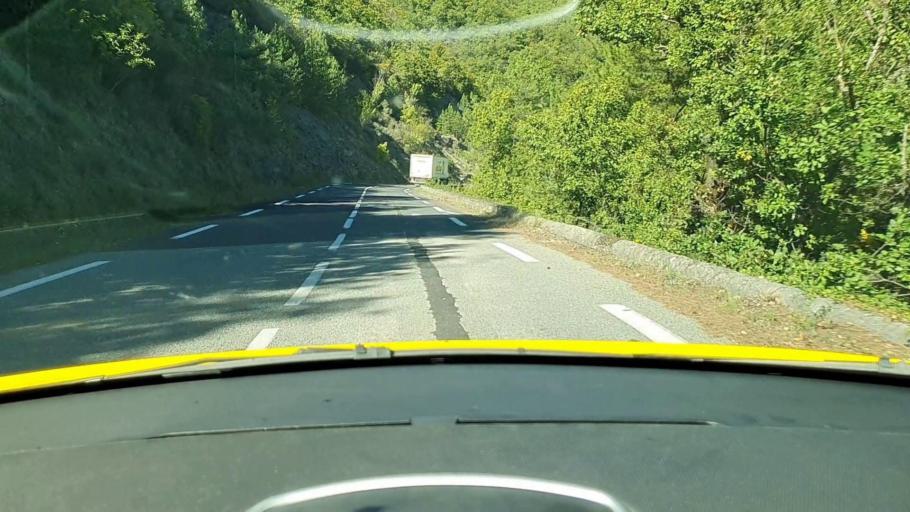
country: FR
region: Languedoc-Roussillon
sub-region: Departement du Gard
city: Le Vigan
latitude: 43.9748
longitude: 3.4617
